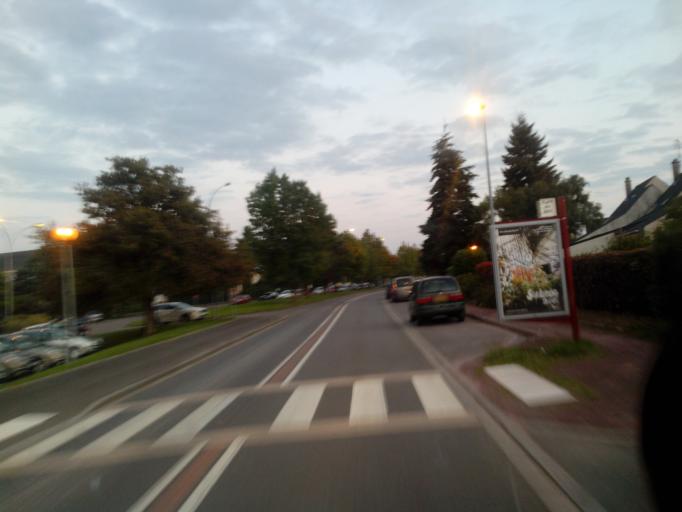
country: FR
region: Brittany
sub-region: Departement d'Ille-et-Vilaine
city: Montfort-sur-Meu
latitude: 48.1436
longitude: -1.9651
